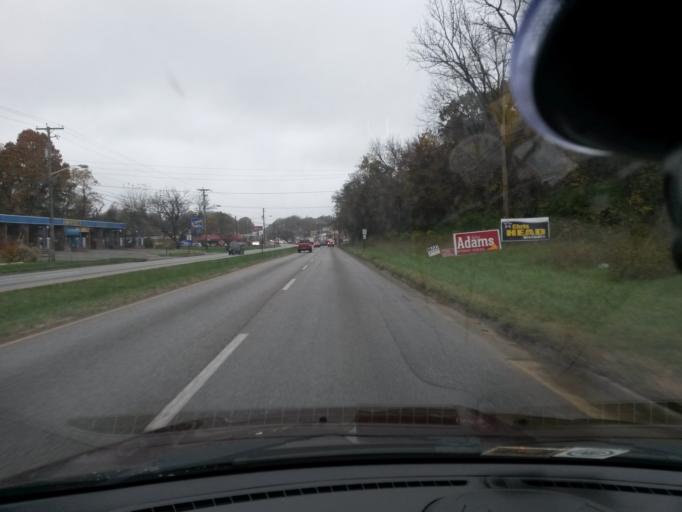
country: US
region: Virginia
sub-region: Roanoke County
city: Vinton
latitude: 37.2923
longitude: -79.9069
